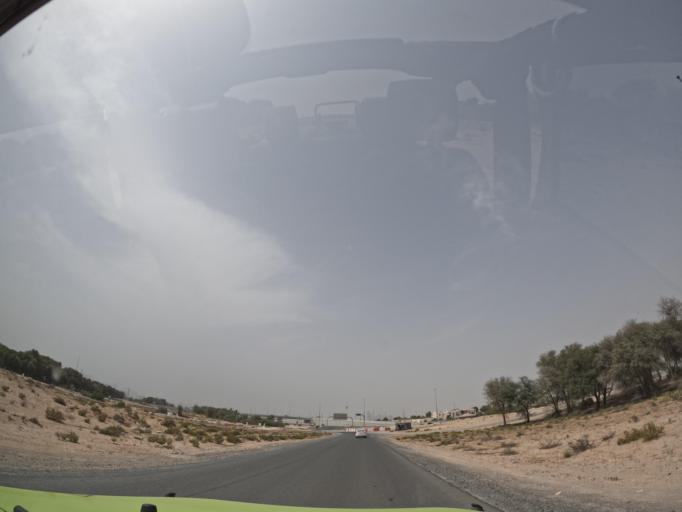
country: AE
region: Dubai
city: Dubai
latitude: 25.1465
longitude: 55.3408
